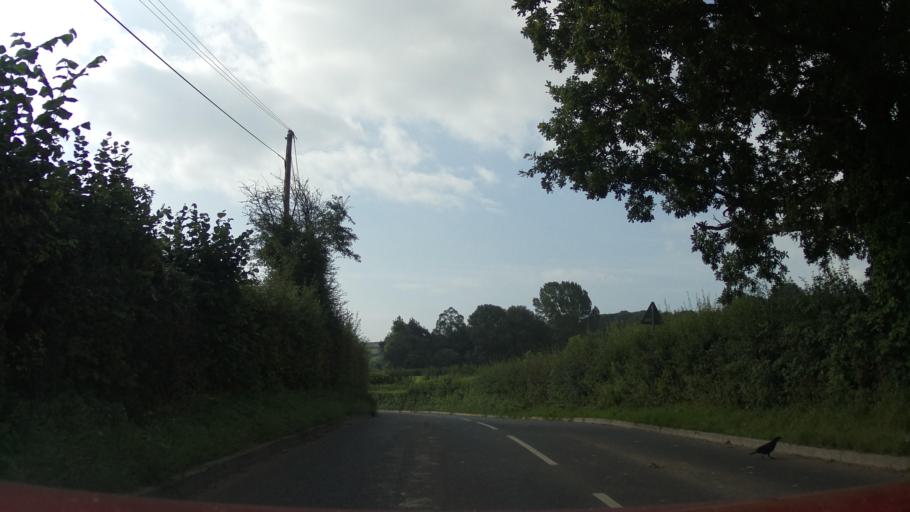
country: GB
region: England
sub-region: North Somerset
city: Long Ashton
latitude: 51.4185
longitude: -2.6900
